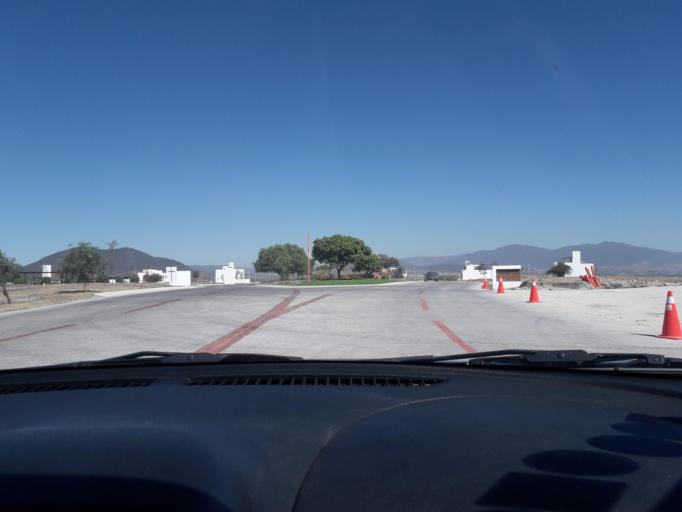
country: MX
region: Queretaro
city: Santa Rosa Jauregui
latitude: 20.7353
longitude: -100.4823
